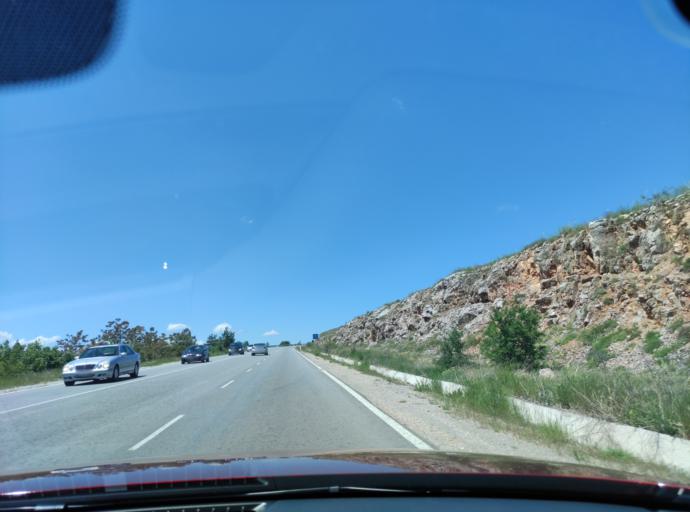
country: BG
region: Sofiya
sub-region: Obshtina Kostinbrod
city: Kostinbrod
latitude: 42.8906
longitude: 23.1584
